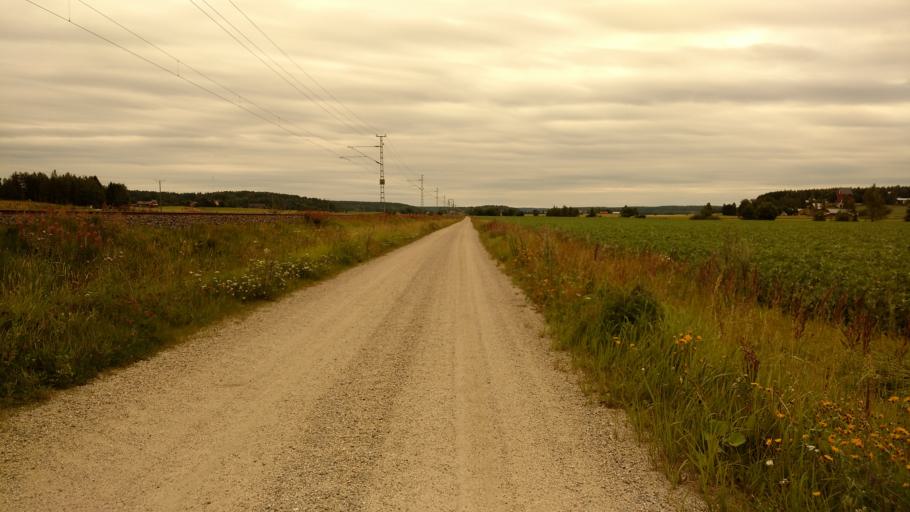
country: FI
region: Varsinais-Suomi
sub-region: Turku
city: Paimio
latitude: 60.4222
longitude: 22.8205
